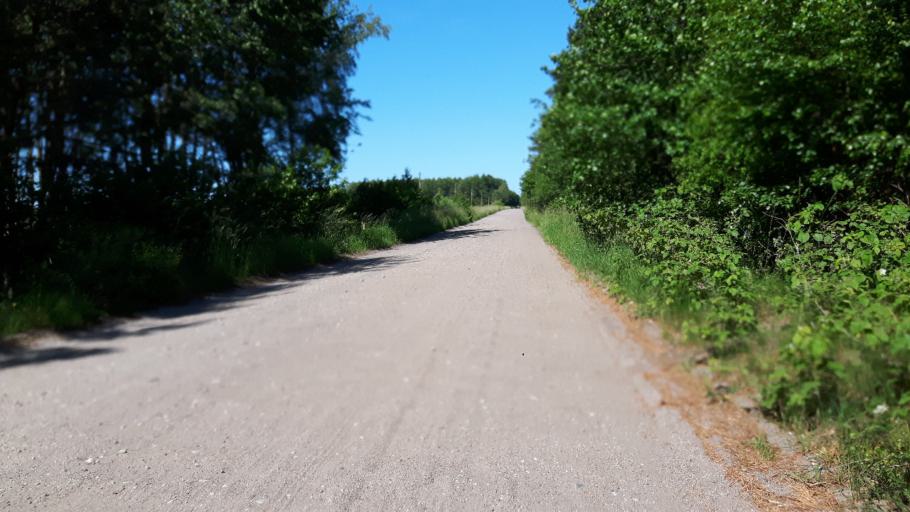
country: PL
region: Pomeranian Voivodeship
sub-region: Powiat slupski
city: Glowczyce
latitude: 54.6846
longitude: 17.4400
